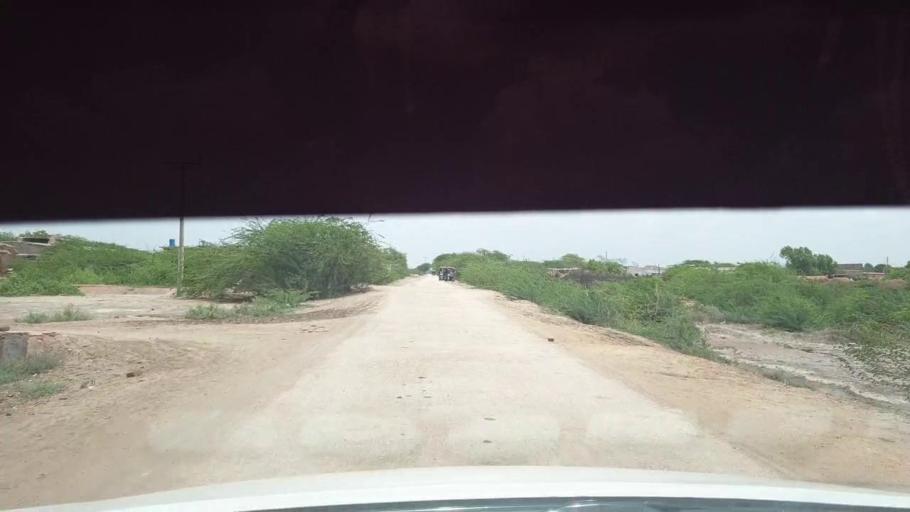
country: PK
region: Sindh
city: Kadhan
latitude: 24.4651
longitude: 69.0121
